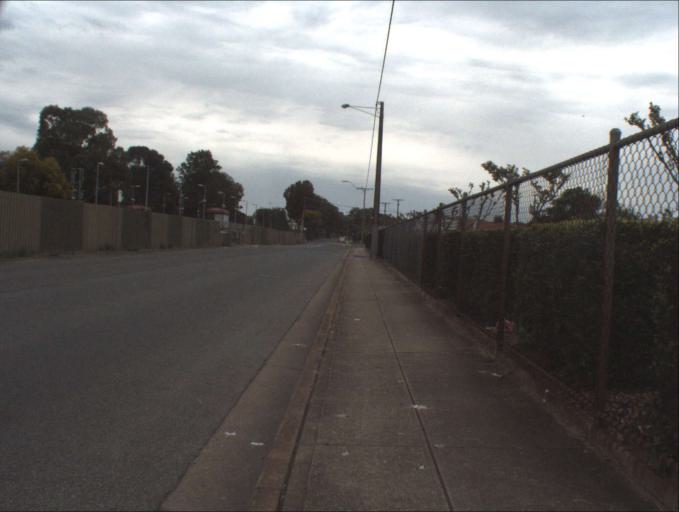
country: AU
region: South Australia
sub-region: Prospect
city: Prospect
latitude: -34.8840
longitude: 138.5829
